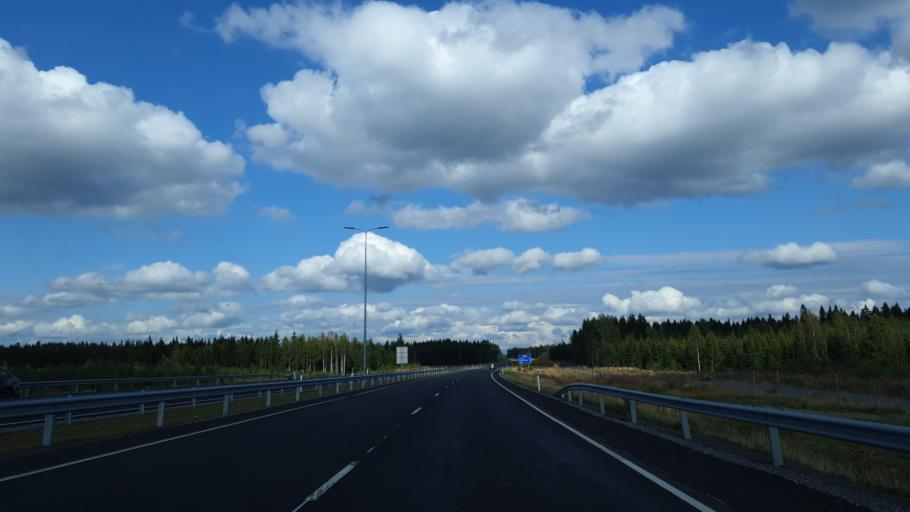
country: FI
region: Southern Savonia
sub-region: Mikkeli
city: Mikkeli
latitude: 61.7184
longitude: 27.3458
